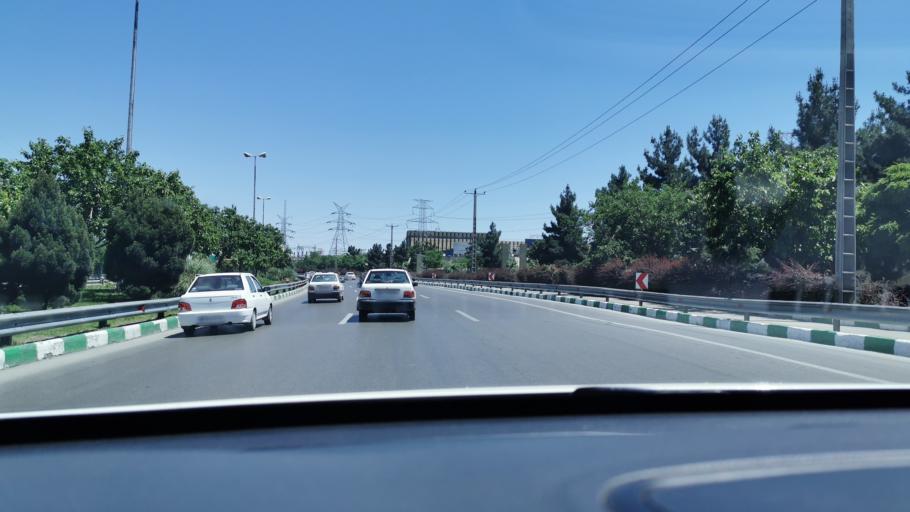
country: IR
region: Razavi Khorasan
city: Mashhad
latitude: 36.2580
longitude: 59.5887
